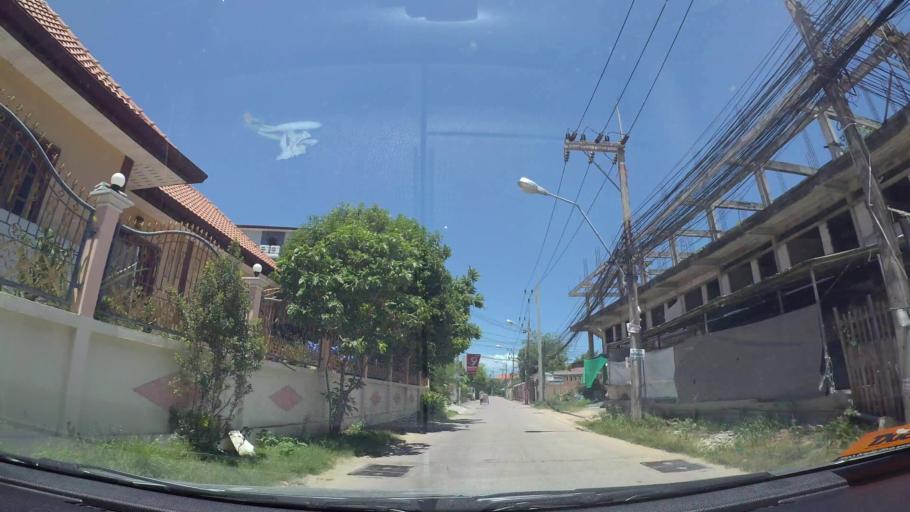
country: TH
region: Chon Buri
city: Phatthaya
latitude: 12.9243
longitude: 100.8962
